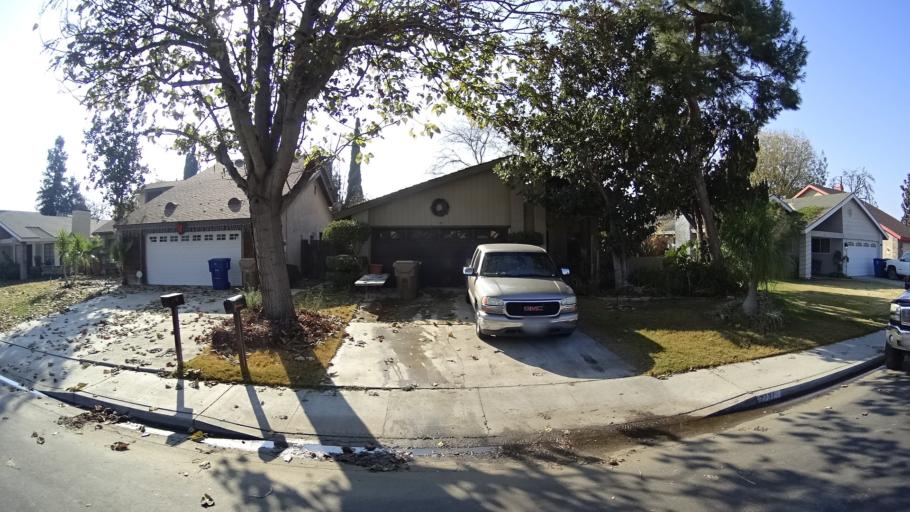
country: US
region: California
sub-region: Kern County
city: Greenacres
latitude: 35.3194
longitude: -119.0885
